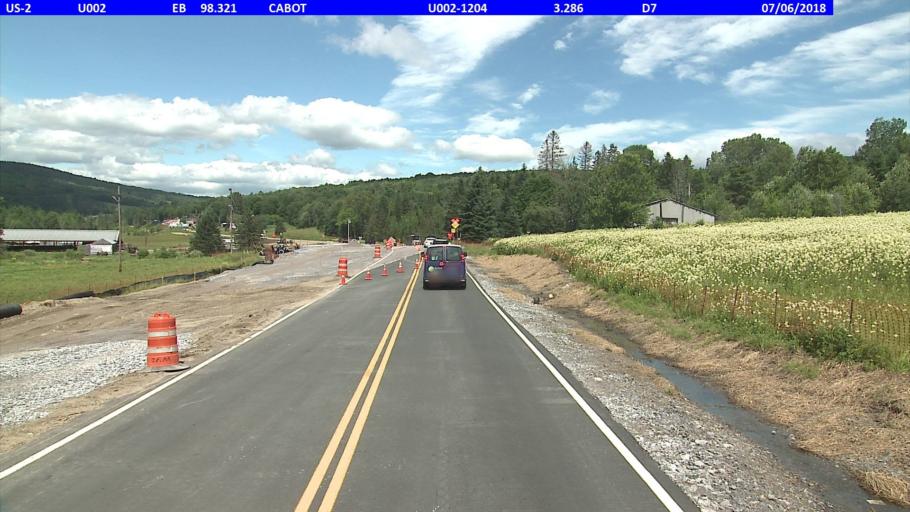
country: US
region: Vermont
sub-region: Caledonia County
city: Hardwick
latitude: 44.3727
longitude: -72.2628
